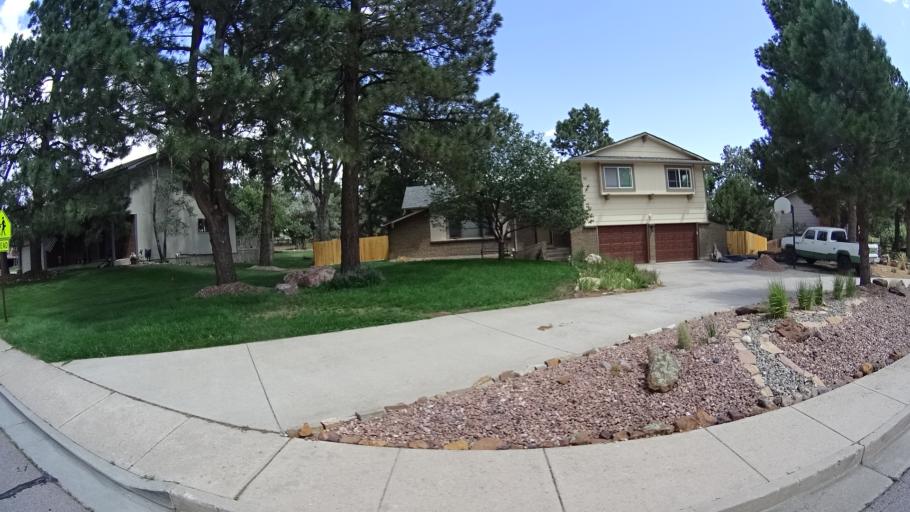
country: US
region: Colorado
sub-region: El Paso County
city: Air Force Academy
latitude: 38.9343
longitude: -104.8334
